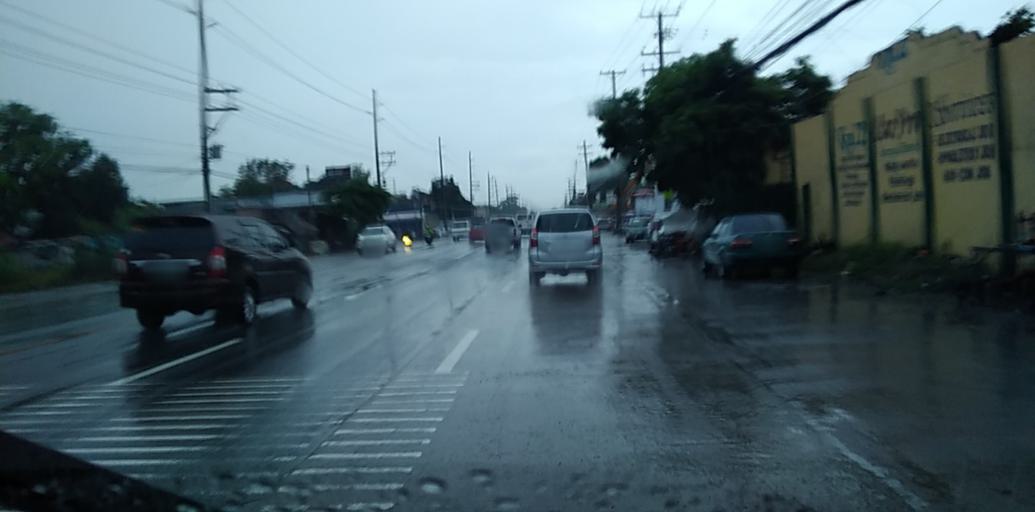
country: PH
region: Central Luzon
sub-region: Province of Pampanga
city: Bulaon
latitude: 15.0616
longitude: 120.6549
